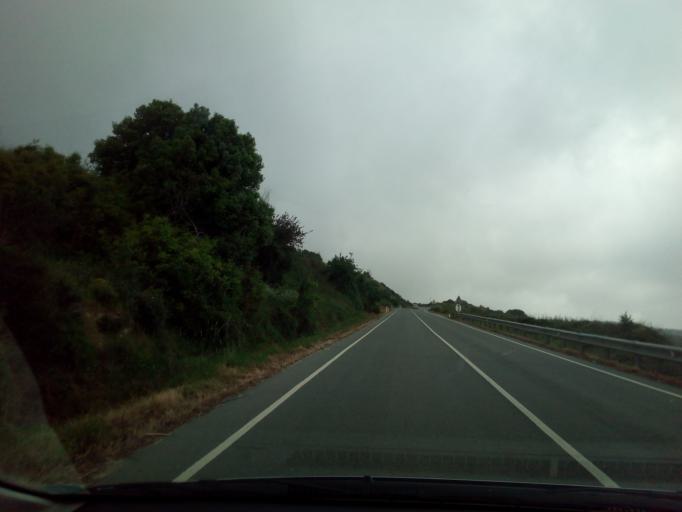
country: CY
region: Pafos
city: Tala
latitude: 34.8975
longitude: 32.4548
